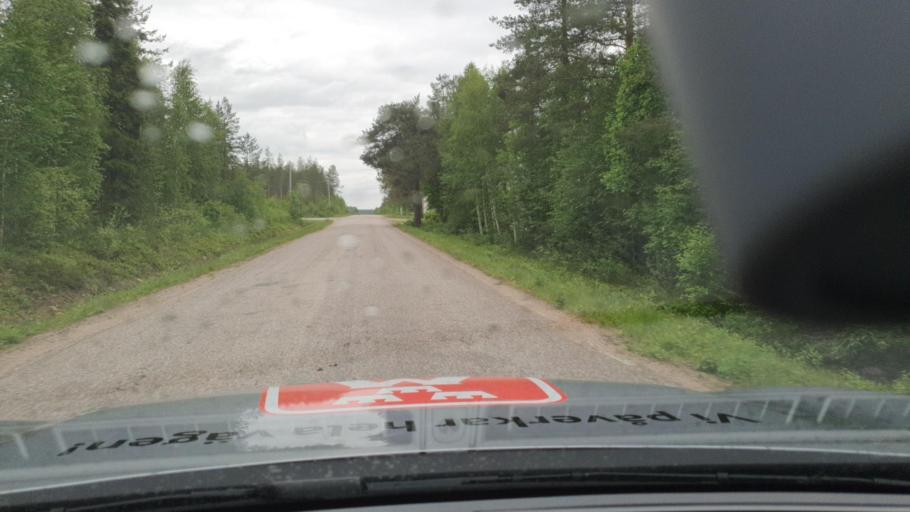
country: SE
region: Norrbotten
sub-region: Overkalix Kommun
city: OEverkalix
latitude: 66.3854
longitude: 22.7929
